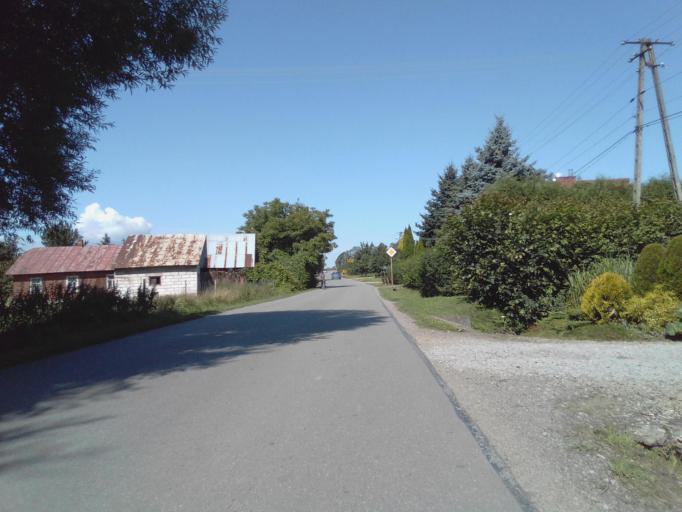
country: PL
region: Subcarpathian Voivodeship
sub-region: Powiat krosnienski
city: Chorkowka
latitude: 49.6064
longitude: 21.6515
